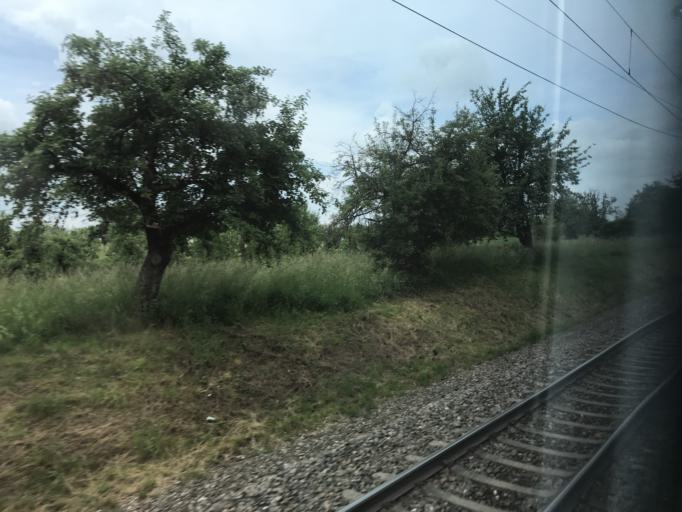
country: DE
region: Baden-Wuerttemberg
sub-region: Regierungsbezirk Stuttgart
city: Gingen an der Fils
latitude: 48.6750
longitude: 9.7725
